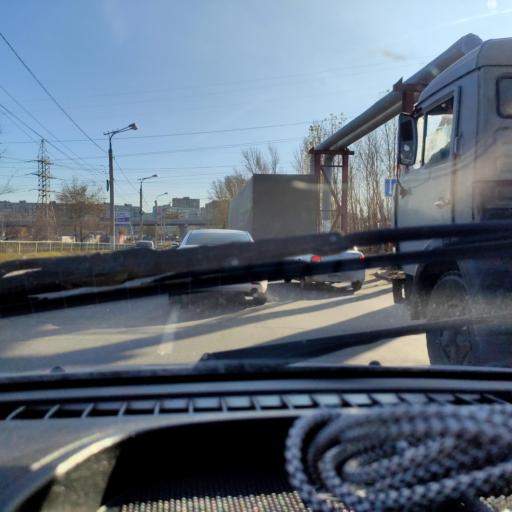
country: RU
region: Samara
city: Zhigulevsk
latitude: 53.4854
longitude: 49.5118
